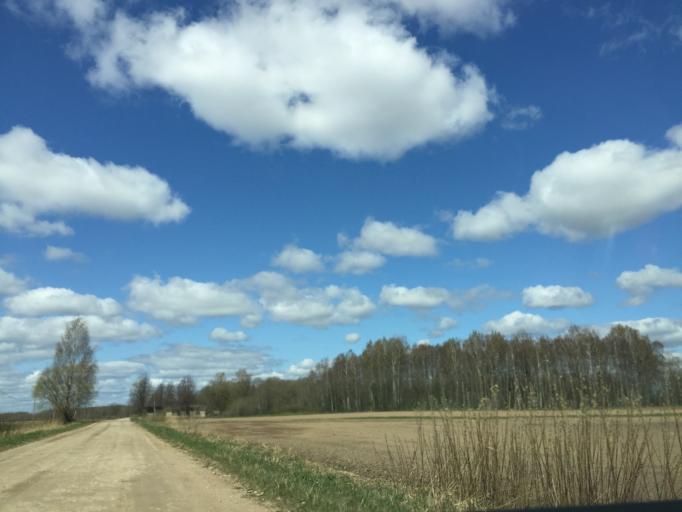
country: LV
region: Vilanu
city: Vilani
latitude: 56.6628
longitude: 27.1101
